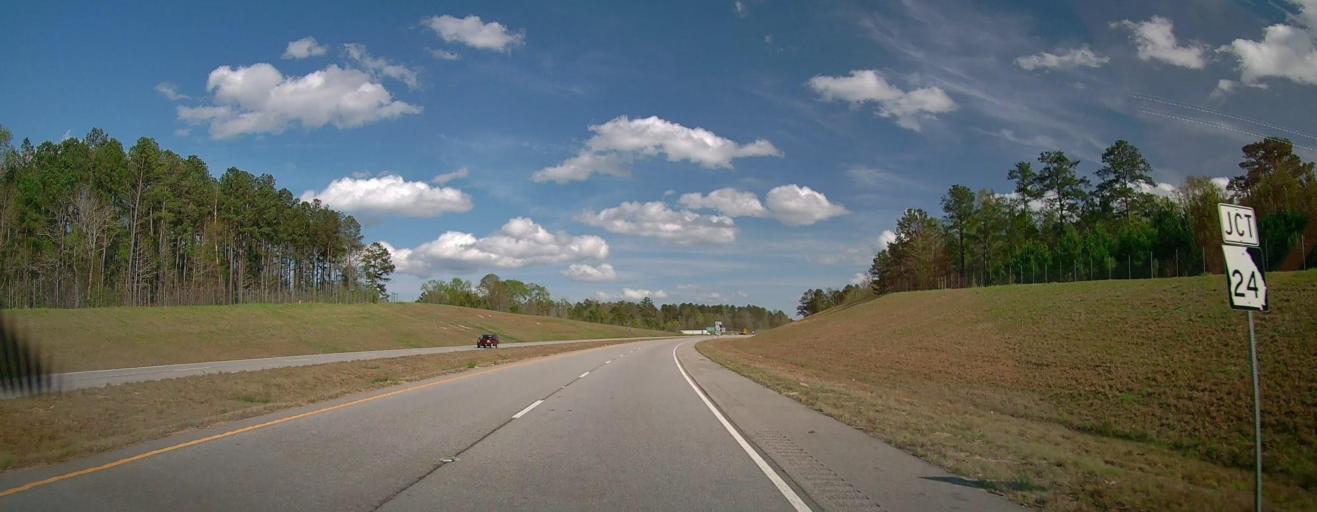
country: US
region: Georgia
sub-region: Baldwin County
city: Hardwick
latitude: 33.0407
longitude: -83.1216
